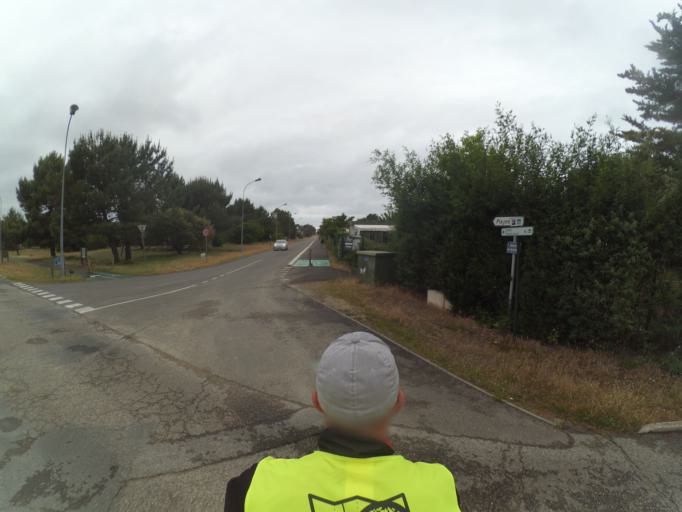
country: FR
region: Aquitaine
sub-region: Departement des Landes
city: Mimizan
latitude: 44.2172
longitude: -1.2818
